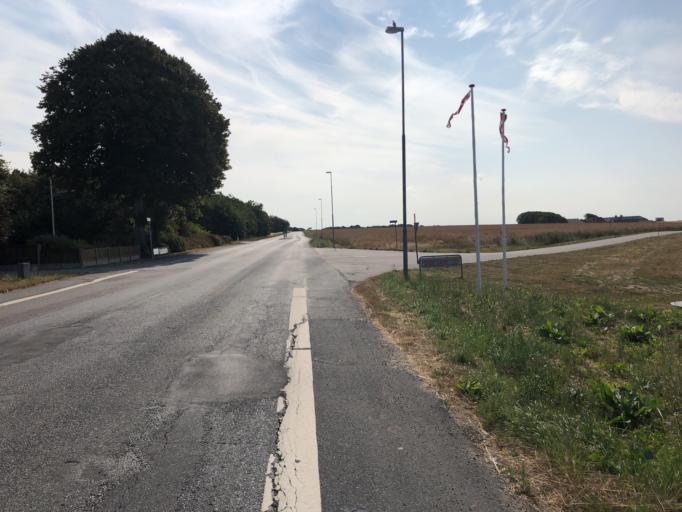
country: DK
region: Central Jutland
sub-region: Holstebro Kommune
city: Vinderup
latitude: 56.5901
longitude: 8.7885
